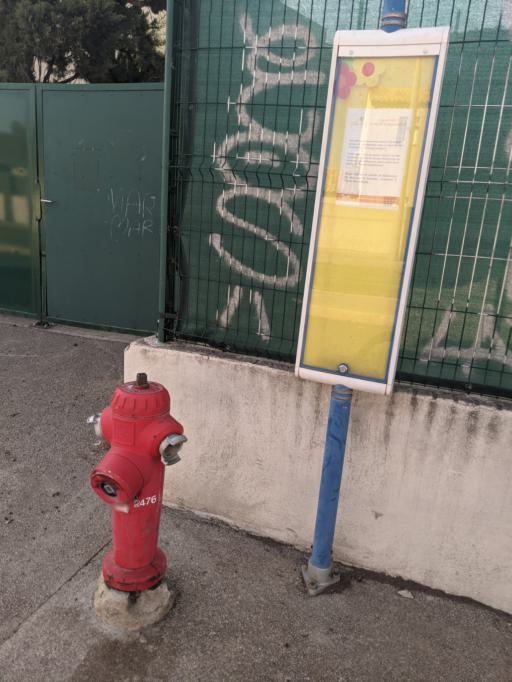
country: FR
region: Languedoc-Roussillon
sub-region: Departement de l'Herault
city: Montpellier
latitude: 43.5880
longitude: 3.8655
